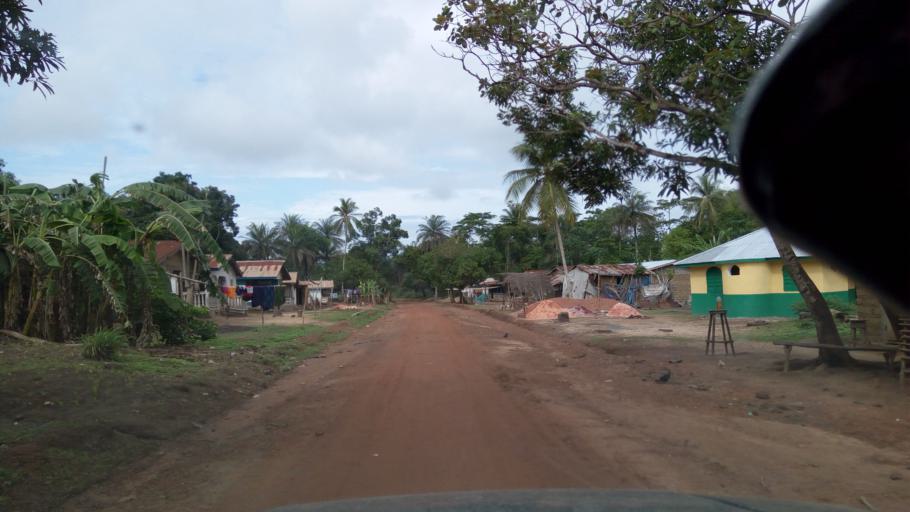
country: SL
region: Northern Province
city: Pepel
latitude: 8.6241
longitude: -13.0334
